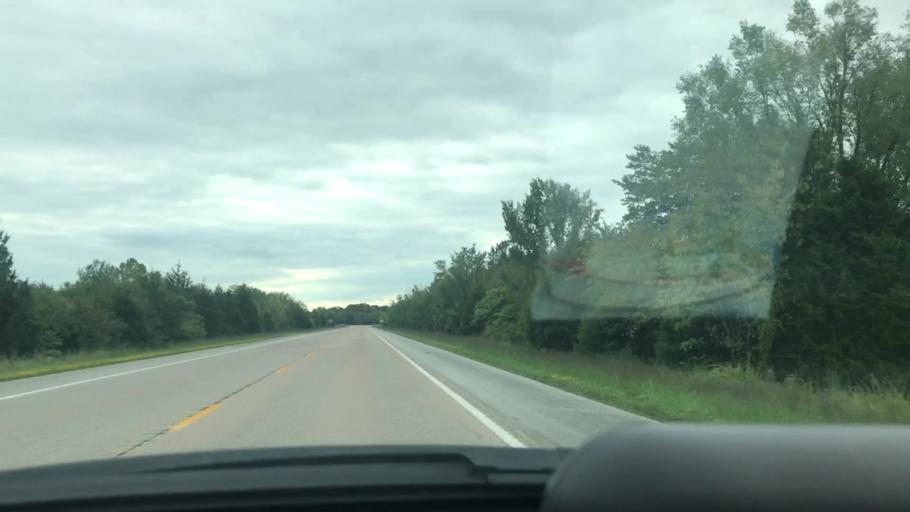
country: US
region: Missouri
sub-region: Benton County
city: Warsaw
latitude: 38.2103
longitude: -93.3368
